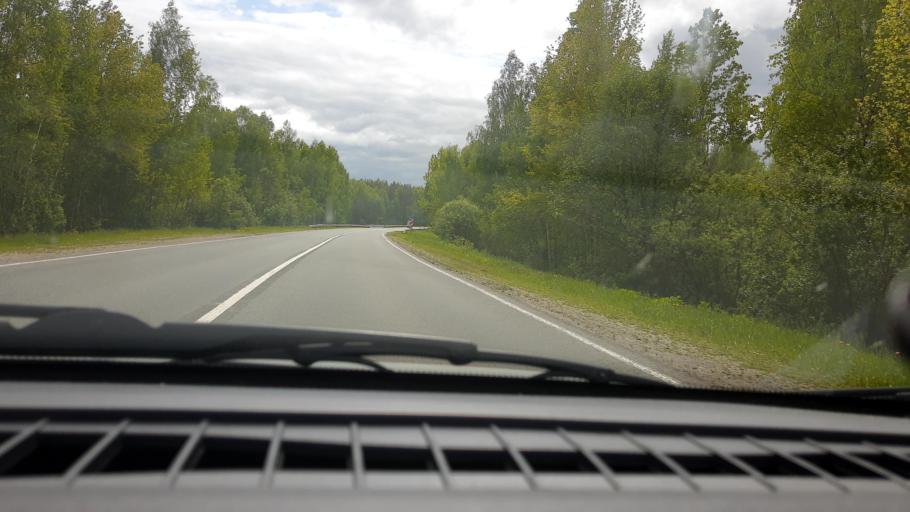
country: RU
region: Nizjnij Novgorod
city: Semenov
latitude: 56.7974
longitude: 44.4599
